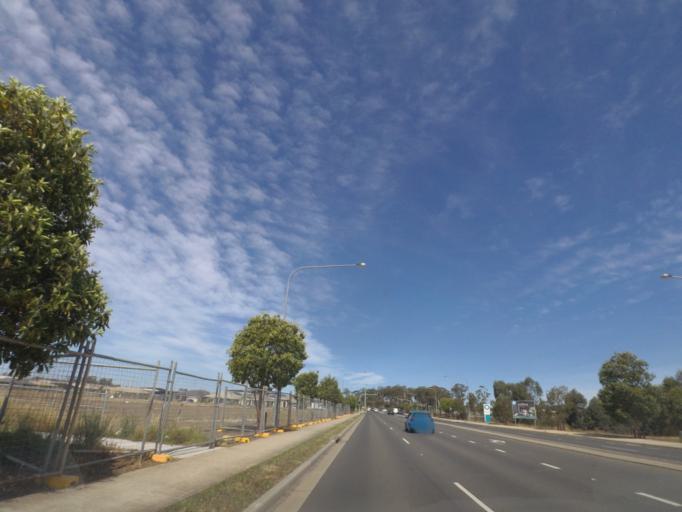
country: AU
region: New South Wales
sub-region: Camden
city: Narellan Vale
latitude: -34.0238
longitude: 150.7695
